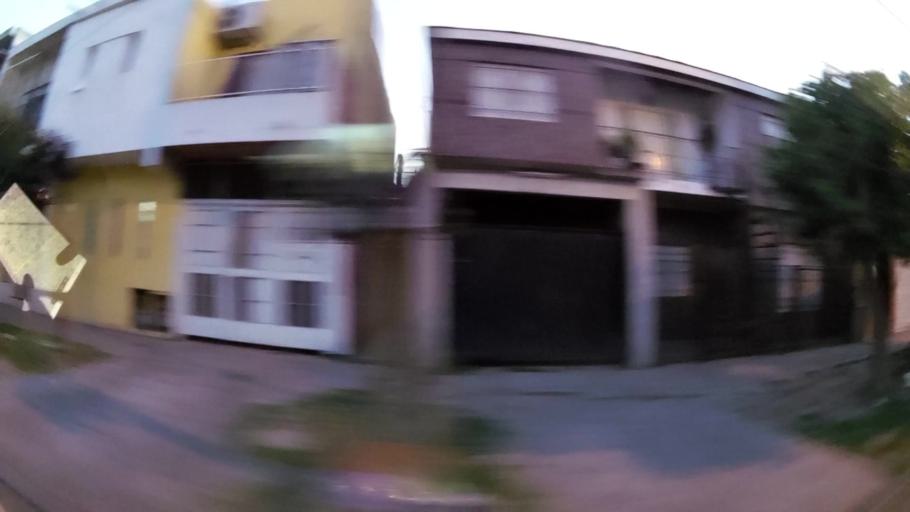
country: AR
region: Buenos Aires
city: San Justo
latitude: -34.7053
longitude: -58.6033
